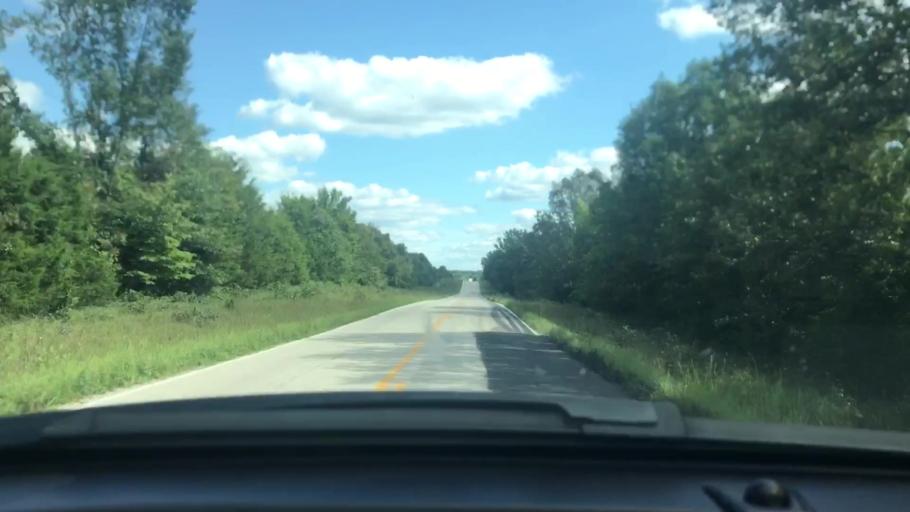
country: US
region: Missouri
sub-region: Wright County
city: Hartville
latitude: 37.3915
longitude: -92.4496
